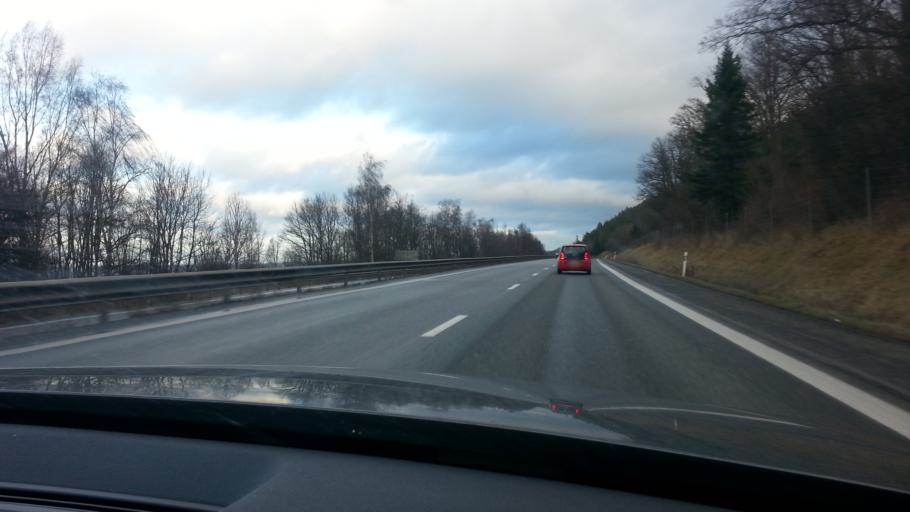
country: SE
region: Joenkoeping
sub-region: Jonkopings Kommun
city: Kaxholmen
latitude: 57.8803
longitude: 14.2786
